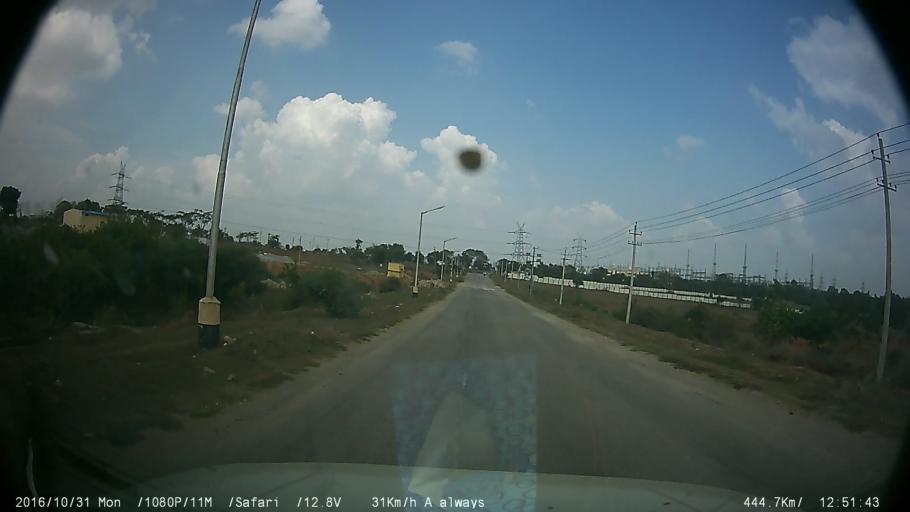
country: IN
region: Karnataka
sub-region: Mysore
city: Mysore
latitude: 12.3649
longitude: 76.5621
